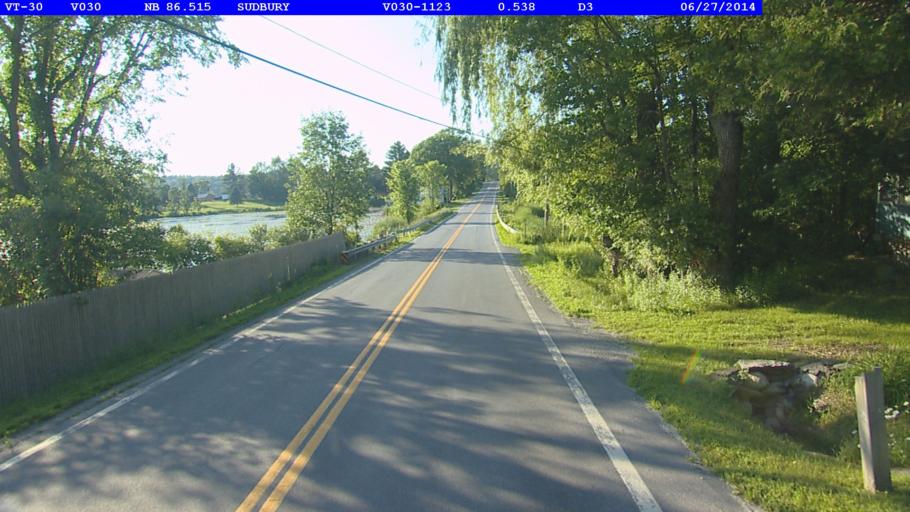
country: US
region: Vermont
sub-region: Rutland County
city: Brandon
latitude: 43.7574
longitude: -73.1936
